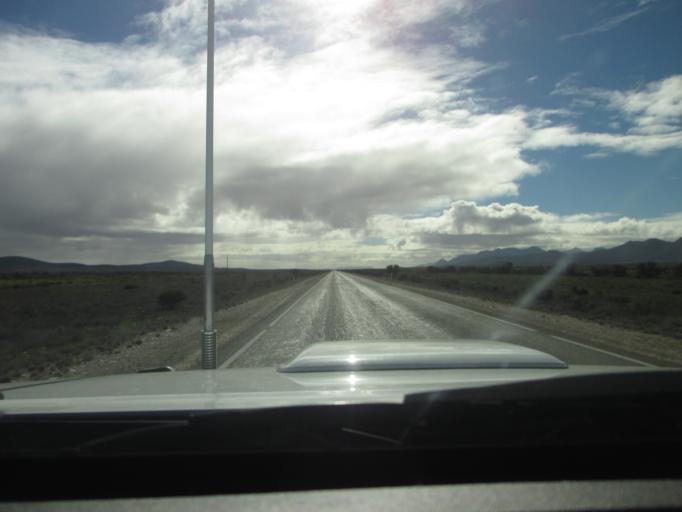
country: AU
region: South Australia
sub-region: Flinders Ranges
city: Quorn
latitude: -31.6812
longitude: 138.3658
